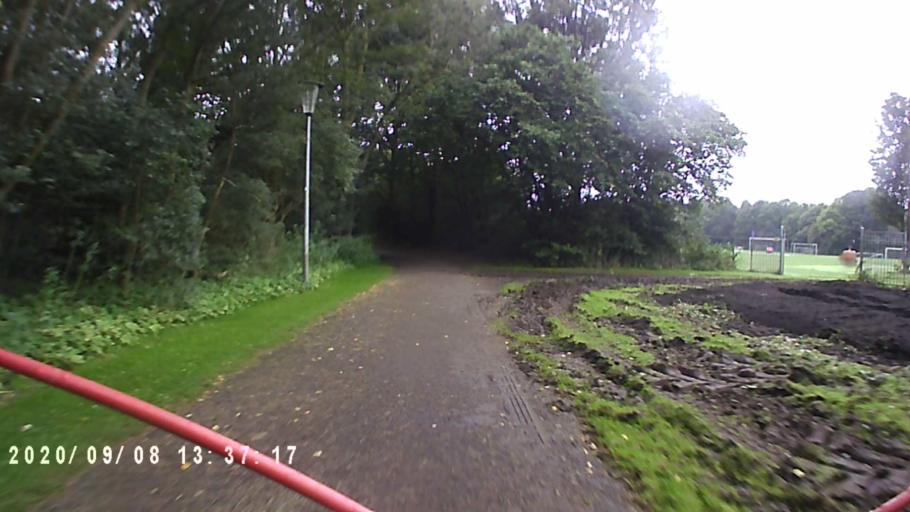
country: NL
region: Groningen
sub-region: Gemeente Veendam
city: Veendam
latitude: 53.1101
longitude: 6.8593
